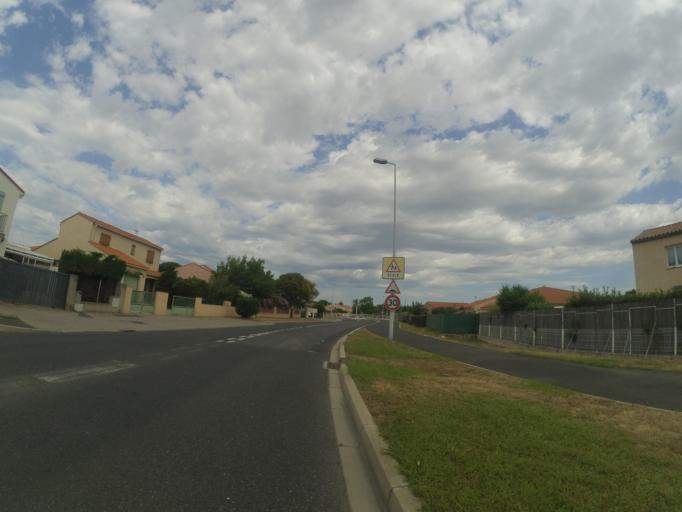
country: FR
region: Languedoc-Roussillon
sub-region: Departement des Pyrenees-Orientales
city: Le Soler
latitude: 42.6804
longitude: 2.8051
